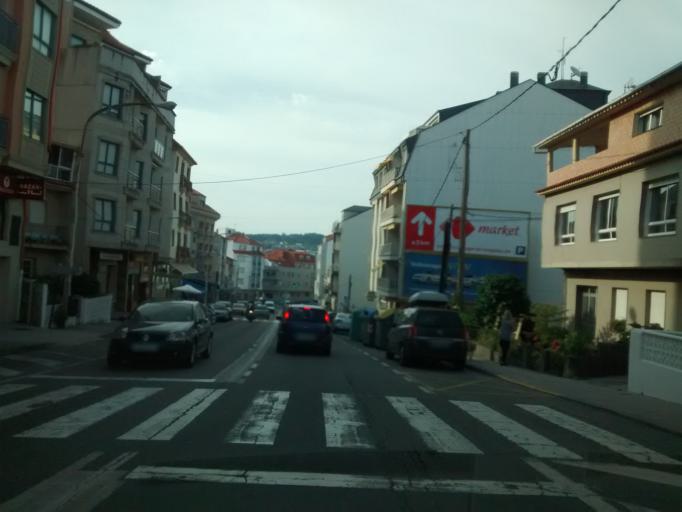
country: ES
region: Galicia
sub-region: Provincia de Pontevedra
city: Sanxenxo
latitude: 42.3940
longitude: -8.8288
